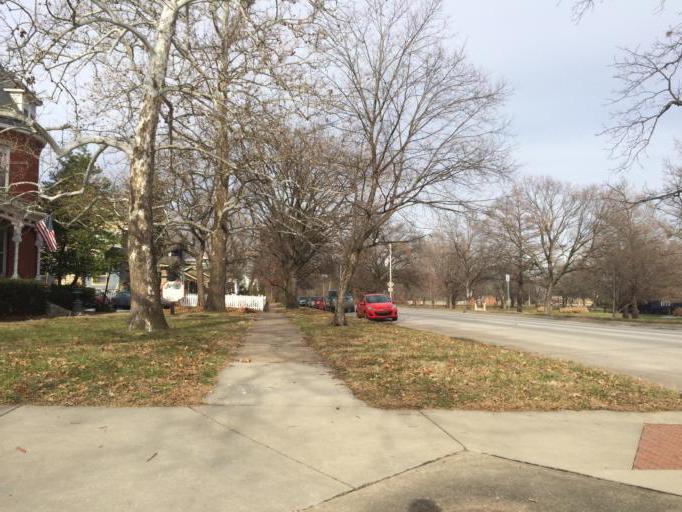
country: US
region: Kansas
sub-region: Douglas County
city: Lawrence
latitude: 38.9713
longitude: -95.2395
